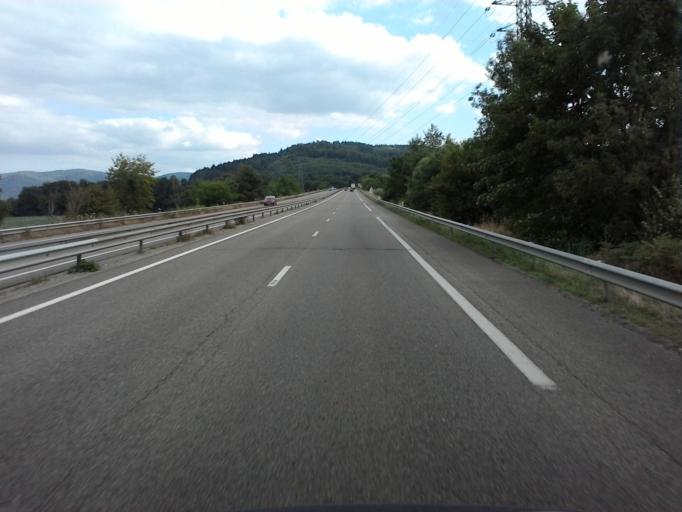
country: FR
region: Lorraine
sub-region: Departement des Vosges
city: Pouxeux
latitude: 48.1013
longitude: 6.5891
